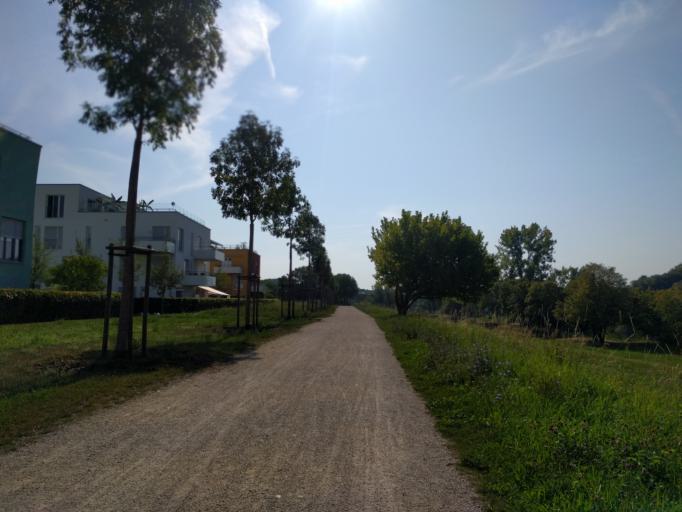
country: DE
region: Bavaria
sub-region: Upper Palatinate
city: Regensburg
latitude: 49.0241
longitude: 12.1086
